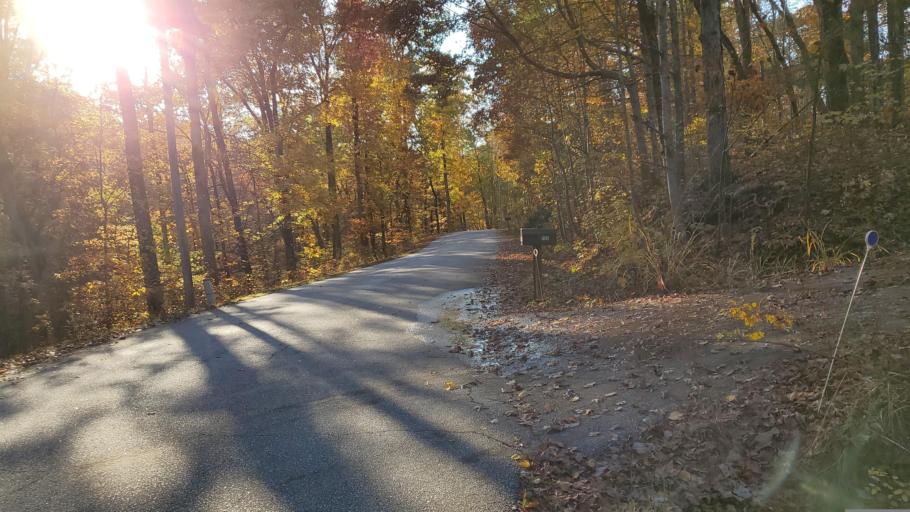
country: US
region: South Carolina
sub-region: Greenville County
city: Tigerville
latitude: 35.0694
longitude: -82.3224
